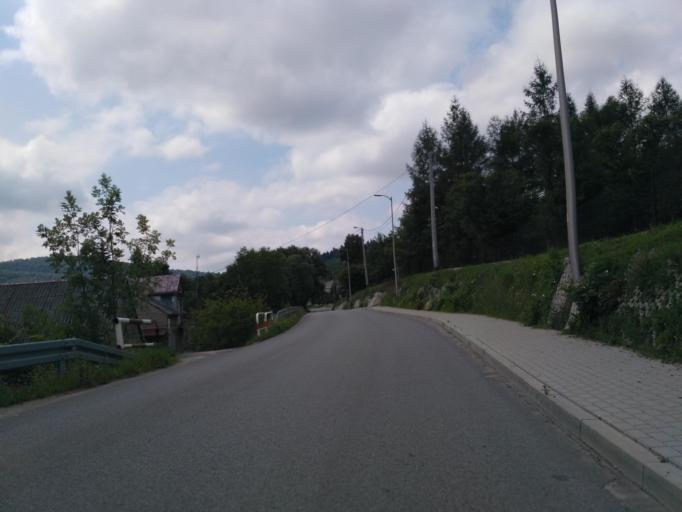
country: PL
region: Subcarpathian Voivodeship
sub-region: Powiat krosnienski
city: Iwonicz-Zdroj
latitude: 49.5794
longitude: 21.8225
